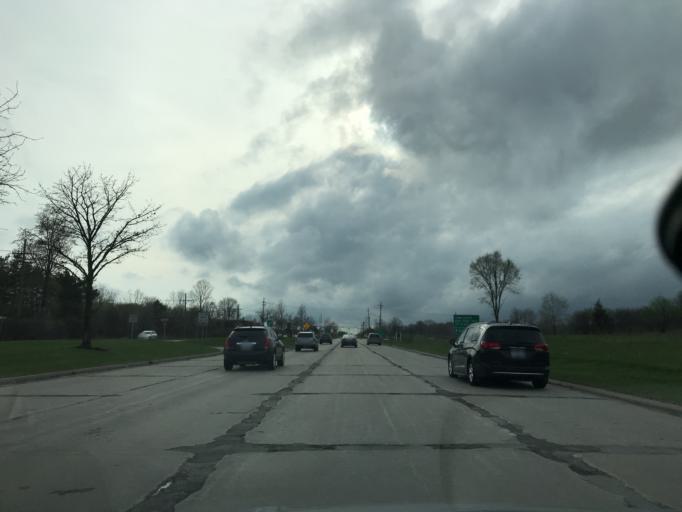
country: US
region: Michigan
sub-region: Oakland County
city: Novi
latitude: 42.4965
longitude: -83.4526
